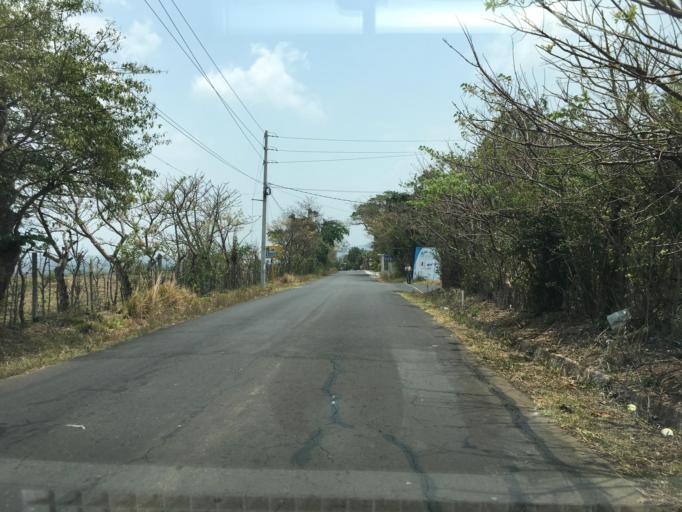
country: GT
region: Santa Rosa
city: Pueblo Nuevo Vinas
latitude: 14.3147
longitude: -90.5476
